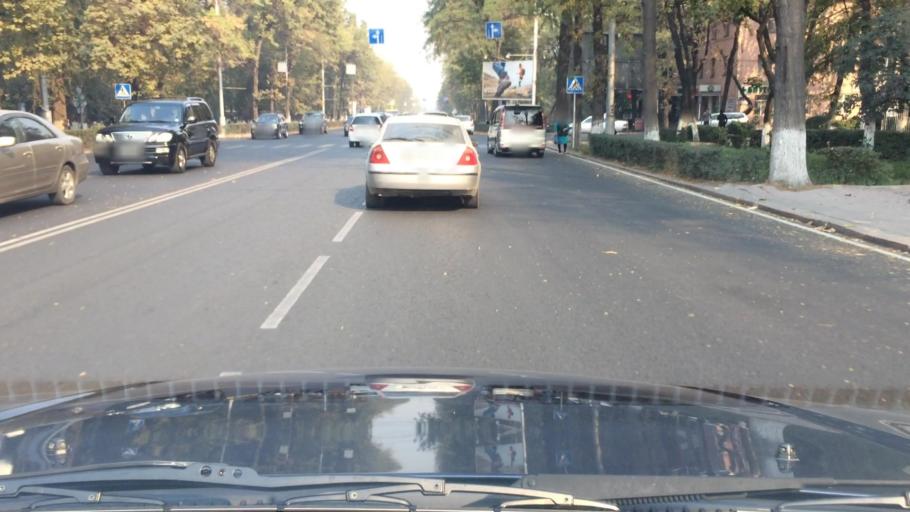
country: KG
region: Chuy
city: Bishkek
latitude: 42.8491
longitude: 74.5864
